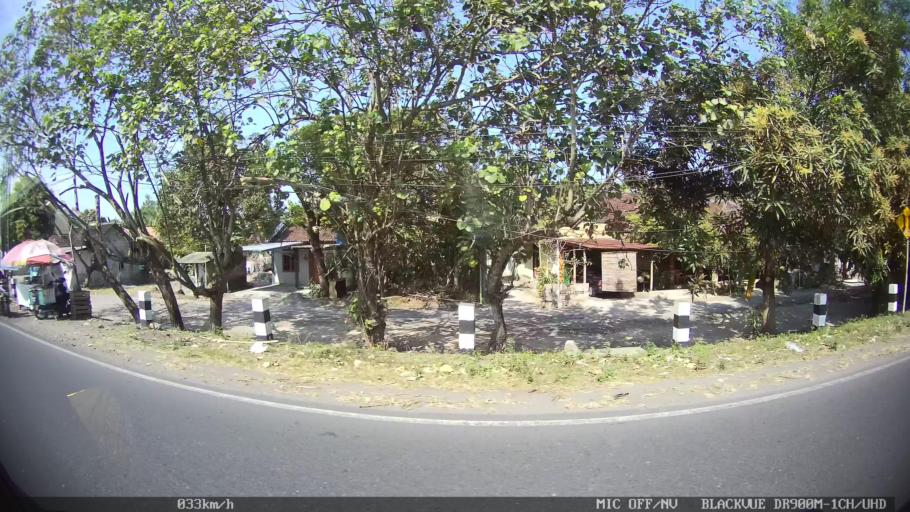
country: ID
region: Daerah Istimewa Yogyakarta
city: Sewon
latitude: -7.9020
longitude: 110.3838
